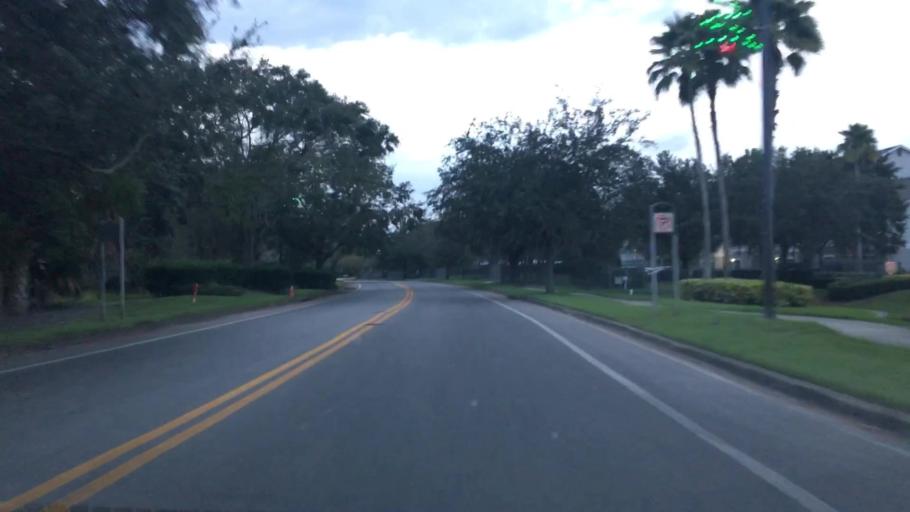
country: US
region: Florida
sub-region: Orange County
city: Conway
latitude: 28.4729
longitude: -81.3044
